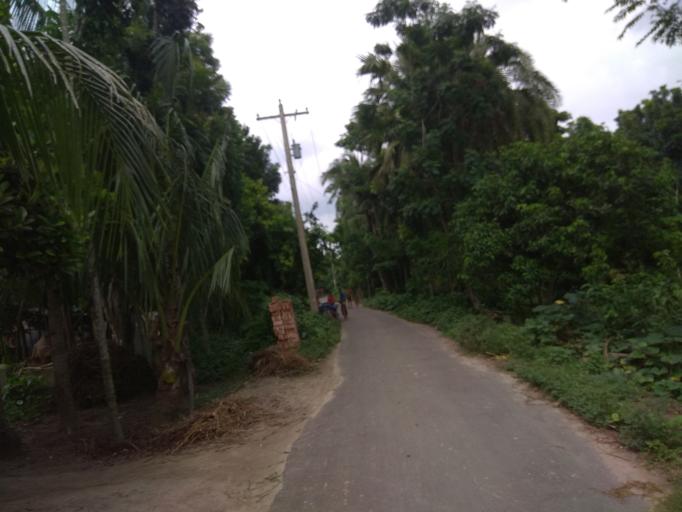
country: BD
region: Dhaka
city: Faridpur
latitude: 23.4887
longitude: 89.9867
